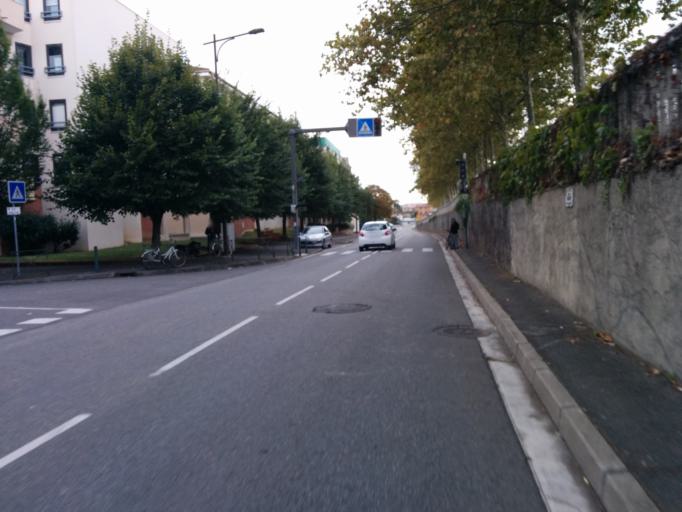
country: FR
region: Midi-Pyrenees
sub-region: Departement de la Haute-Garonne
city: Toulouse
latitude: 43.6034
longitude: 1.4233
